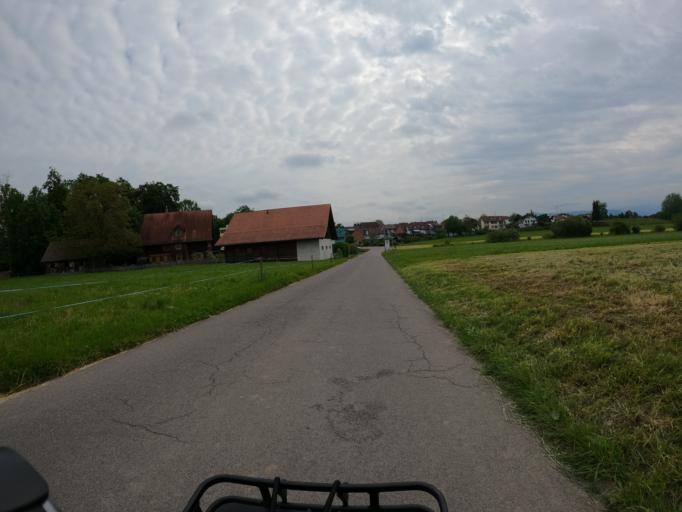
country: CH
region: Zug
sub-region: Zug
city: Hunenberg
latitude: 47.1717
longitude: 8.4232
